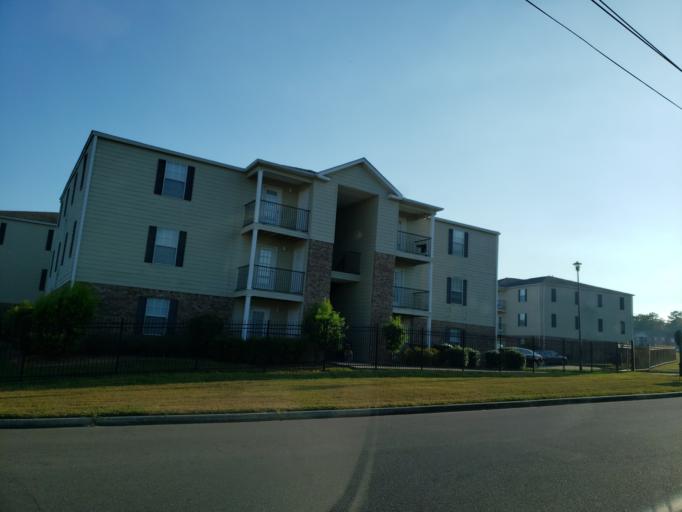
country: US
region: Mississippi
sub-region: Lamar County
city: West Hattiesburg
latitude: 31.3261
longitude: -89.4125
